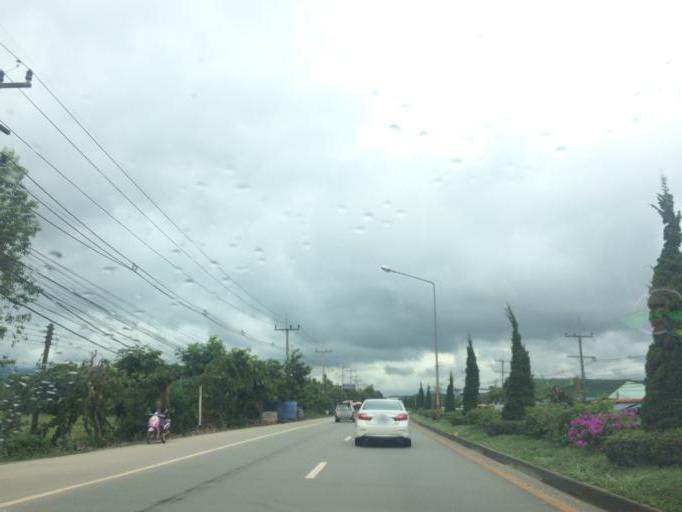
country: TH
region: Chiang Rai
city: Chiang Rai
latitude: 20.0226
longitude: 99.8714
